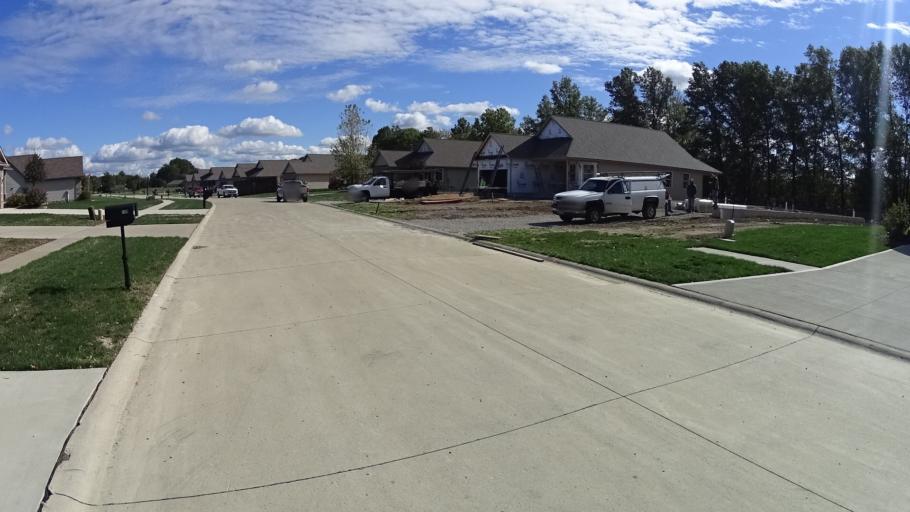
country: US
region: Ohio
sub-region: Lorain County
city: Grafton
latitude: 41.2881
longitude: -82.0701
